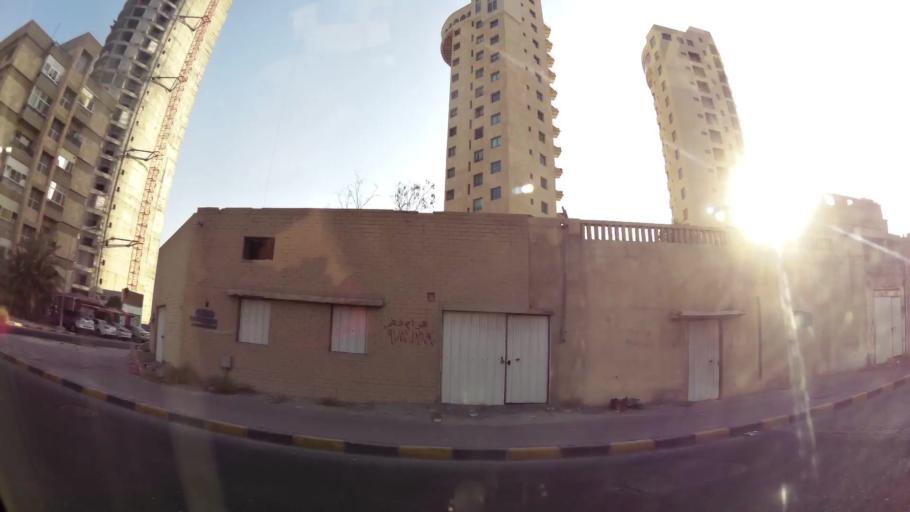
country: KW
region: Muhafazat Hawalli
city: As Salimiyah
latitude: 29.3390
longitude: 48.0628
